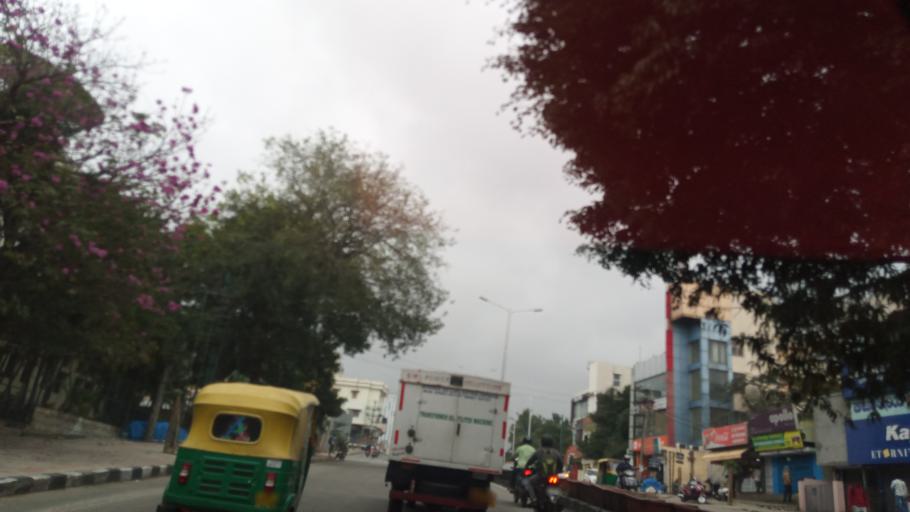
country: IN
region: Karnataka
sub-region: Bangalore Urban
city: Bangalore
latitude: 12.9318
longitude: 77.5420
